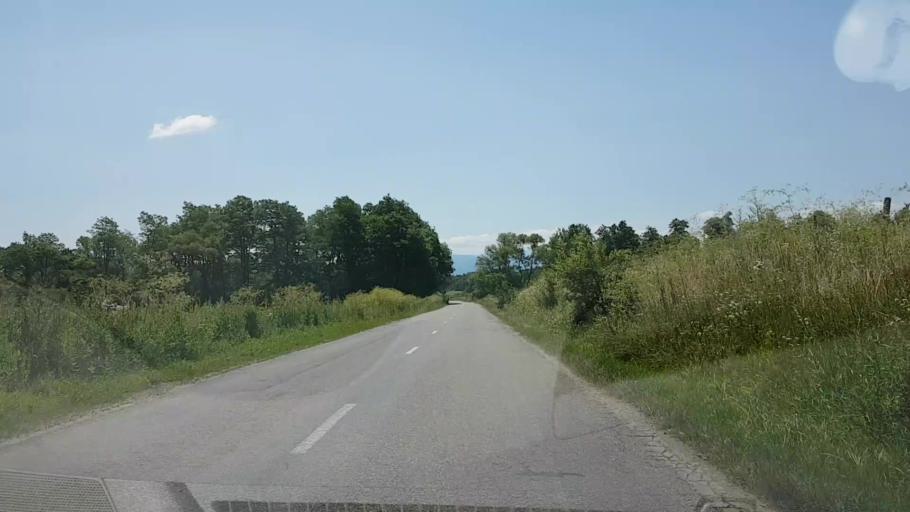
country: RO
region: Brasov
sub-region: Comuna Cincu
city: Cincu
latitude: 45.8804
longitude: 24.8143
